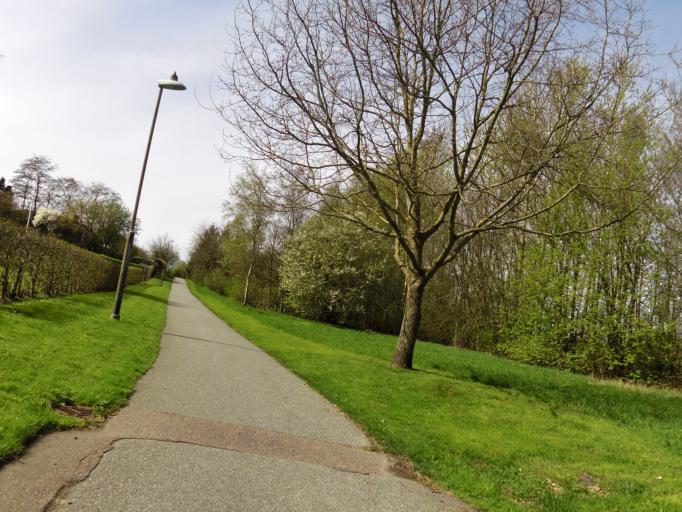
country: DK
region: Central Jutland
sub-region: Skive Kommune
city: Skive
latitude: 56.5844
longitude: 9.0211
